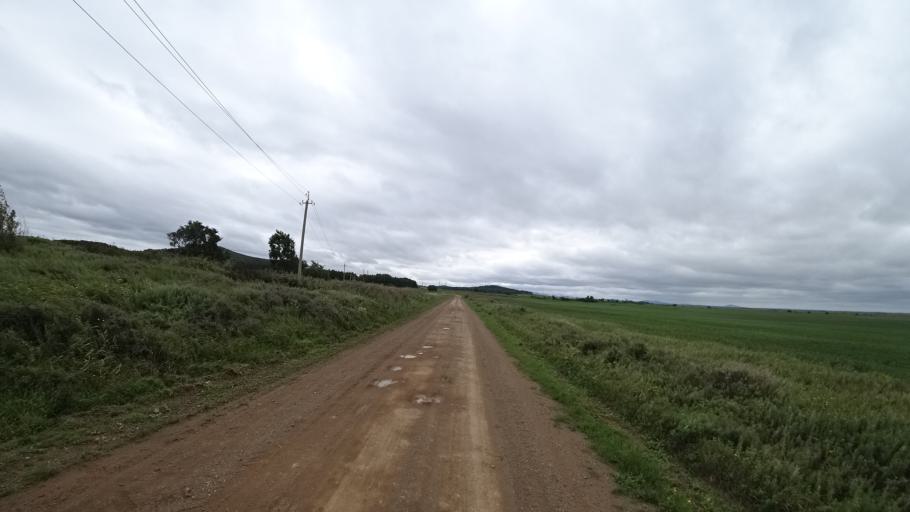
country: RU
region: Primorskiy
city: Chernigovka
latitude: 44.4841
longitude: 132.5739
